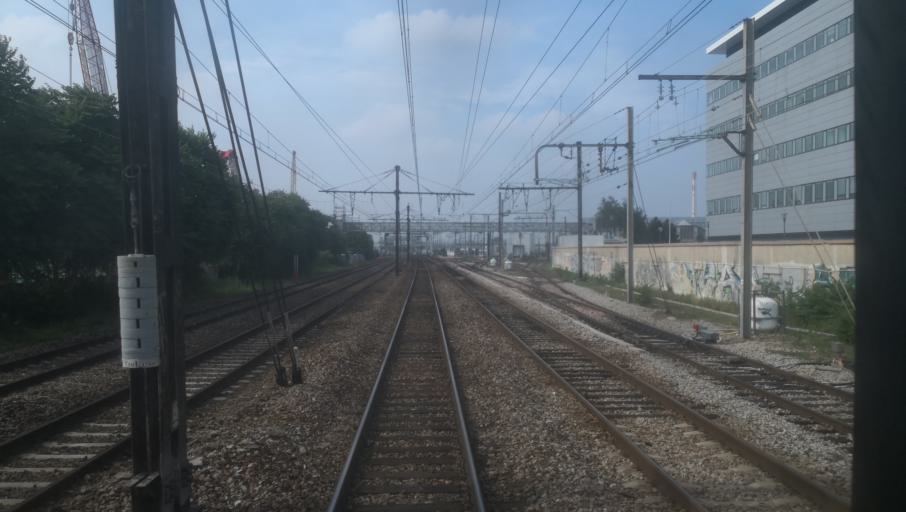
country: FR
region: Ile-de-France
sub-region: Departement du Val-de-Marne
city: Vitry-sur-Seine
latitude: 48.7784
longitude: 2.4101
